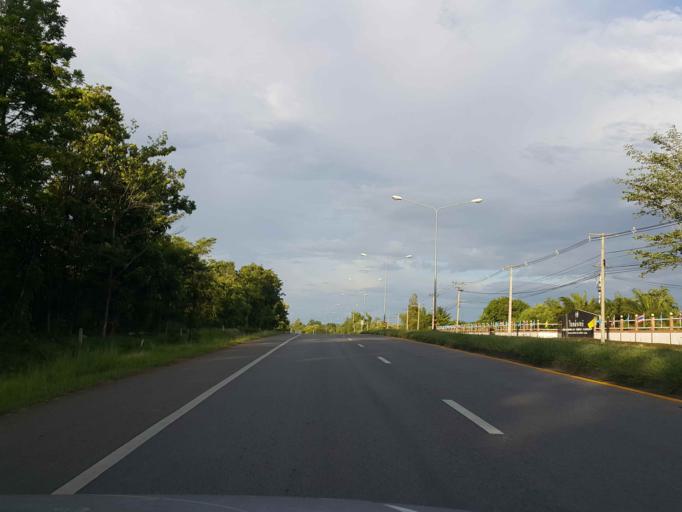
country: TH
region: Sukhothai
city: Ban Dan Lan Hoi
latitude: 16.9280
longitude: 99.4130
